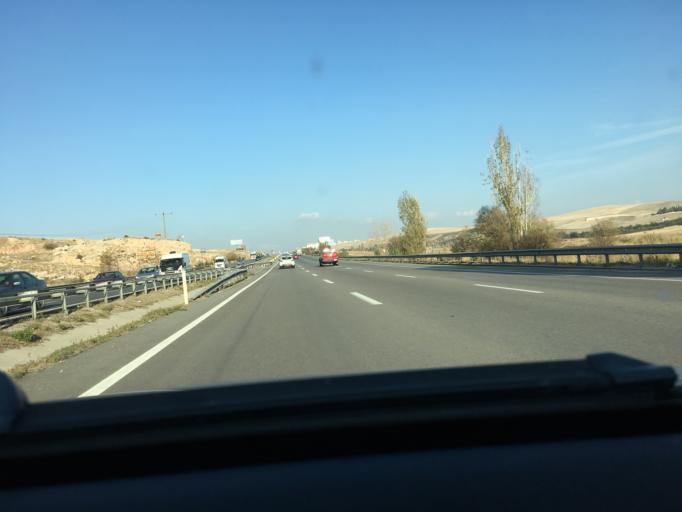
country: TR
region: Ankara
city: Temelli
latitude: 39.7823
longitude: 32.5107
